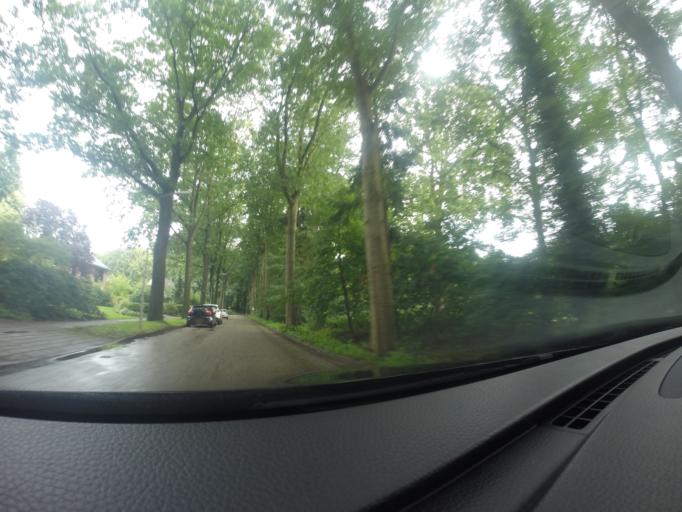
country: NL
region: Gelderland
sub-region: Gemeente Lochem
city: Lochem
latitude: 52.1519
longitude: 6.4050
